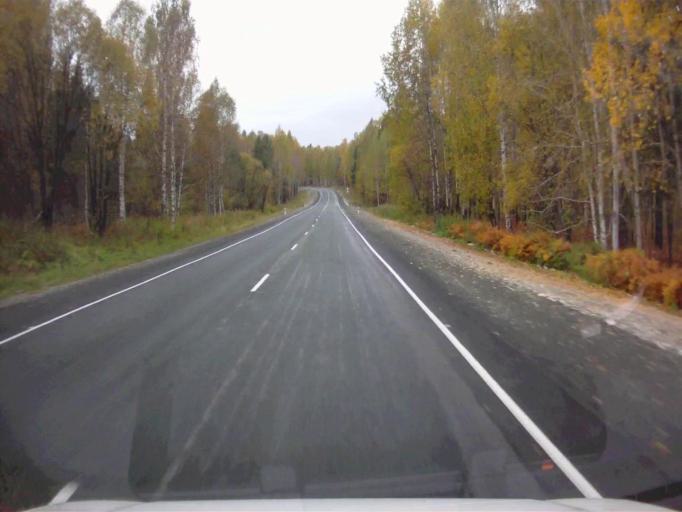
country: RU
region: Chelyabinsk
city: Nyazepetrovsk
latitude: 56.0644
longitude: 59.7205
